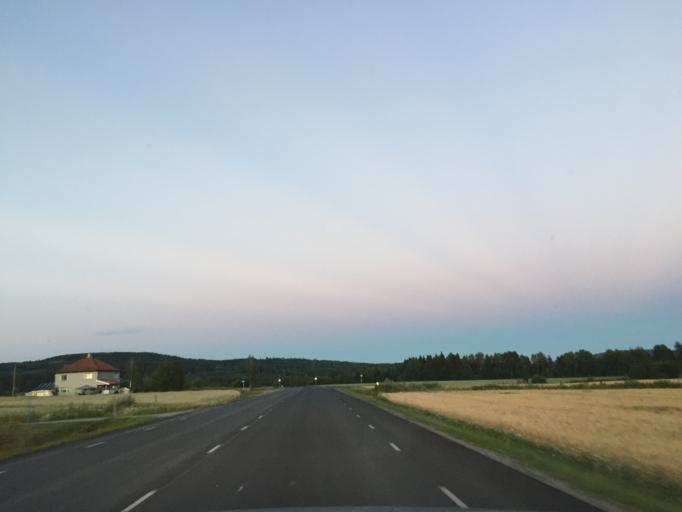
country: NO
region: Hedmark
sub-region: Kongsvinger
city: Spetalen
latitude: 60.2313
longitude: 11.8250
